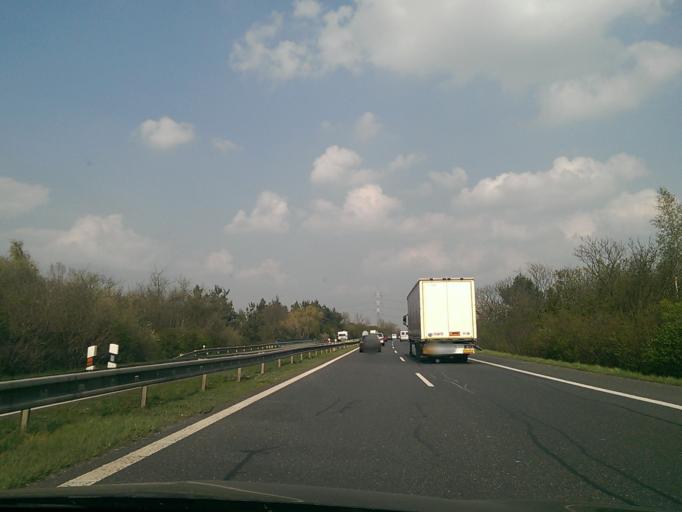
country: CZ
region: Central Bohemia
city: Benatky nad Jizerou
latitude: 50.2480
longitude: 14.7523
